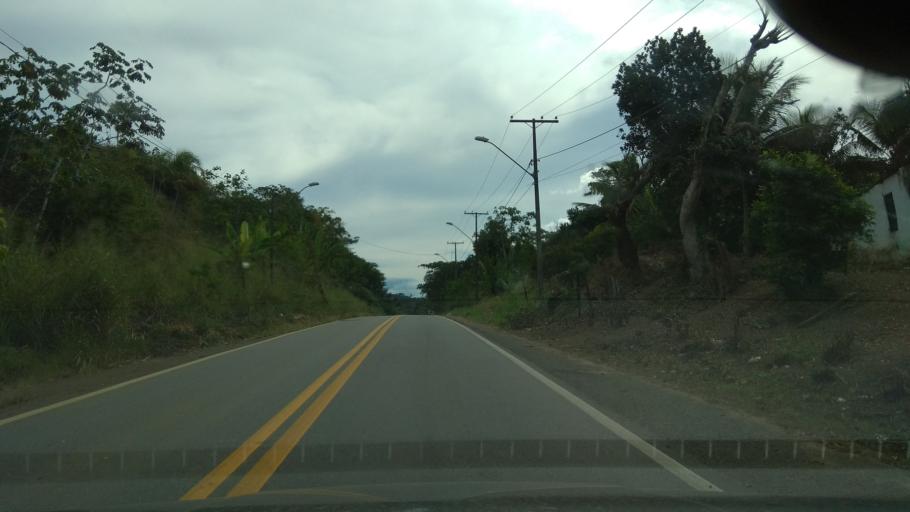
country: BR
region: Bahia
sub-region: Ubata
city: Ubata
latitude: -14.1965
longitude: -39.5431
